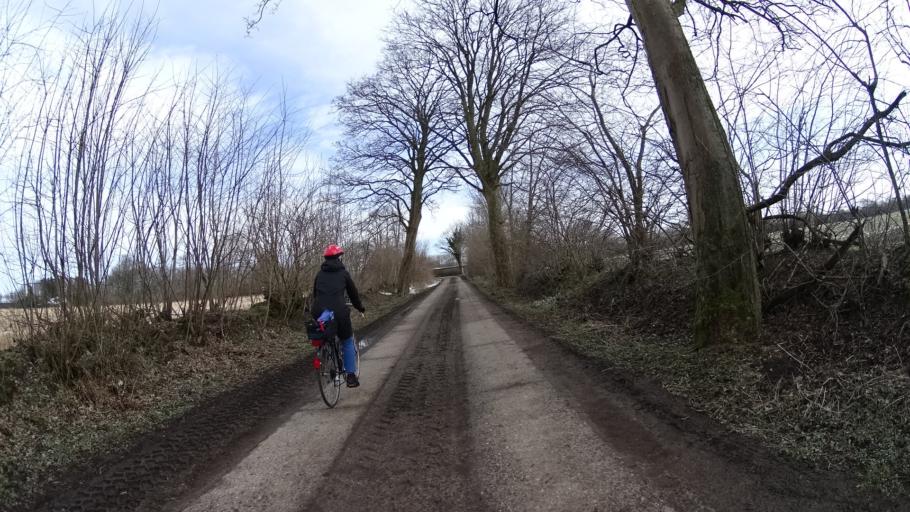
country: DE
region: Schleswig-Holstein
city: Rendswuhren
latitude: 54.0692
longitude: 10.1785
